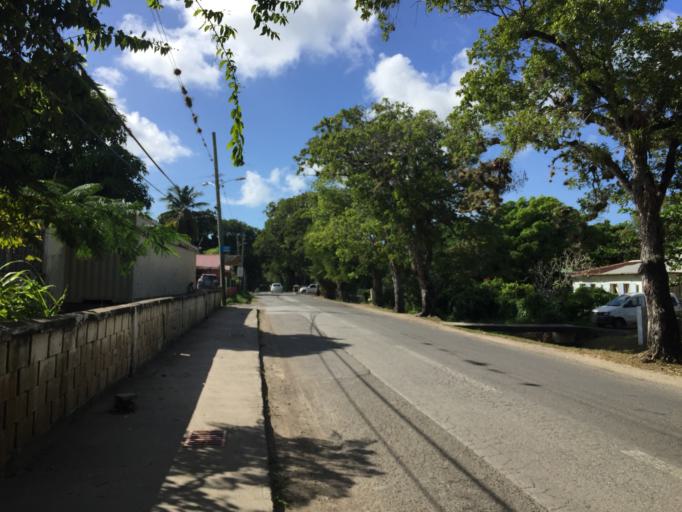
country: AG
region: Saint John
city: Saint John's
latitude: 17.1257
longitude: -61.8409
